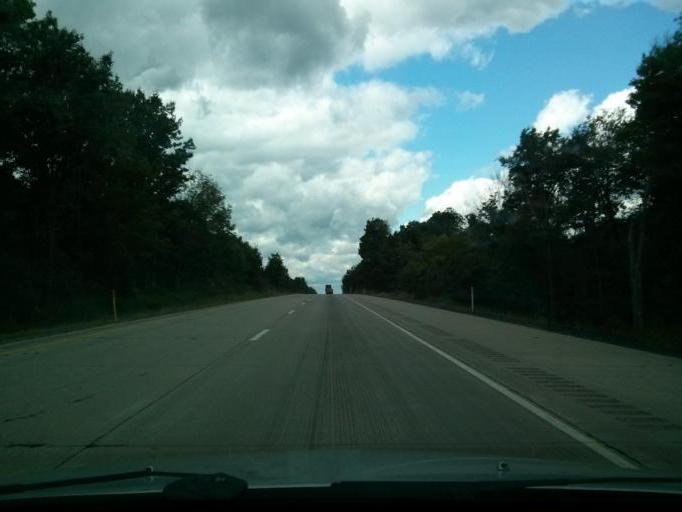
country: US
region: Pennsylvania
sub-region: Jefferson County
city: Reynoldsville
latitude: 41.1526
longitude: -78.9132
